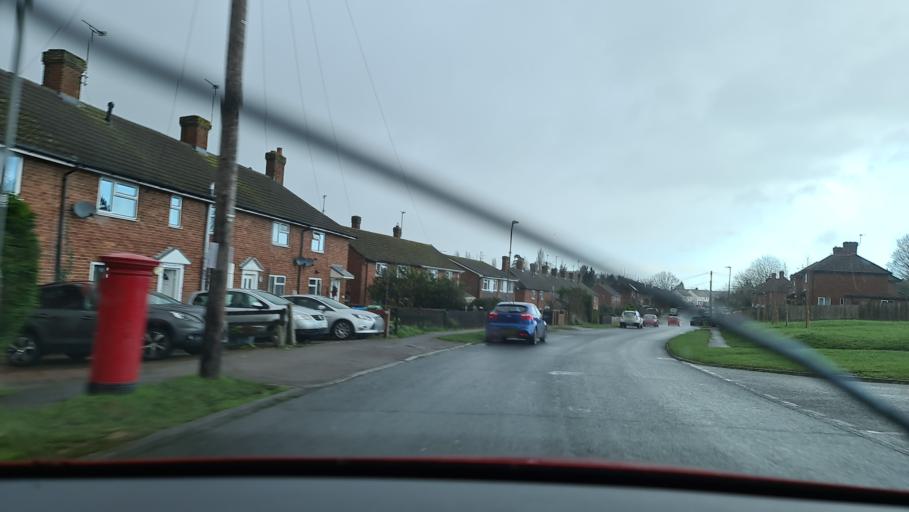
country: GB
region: England
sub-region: Buckinghamshire
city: Buckingham
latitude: 52.0029
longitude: -0.9921
